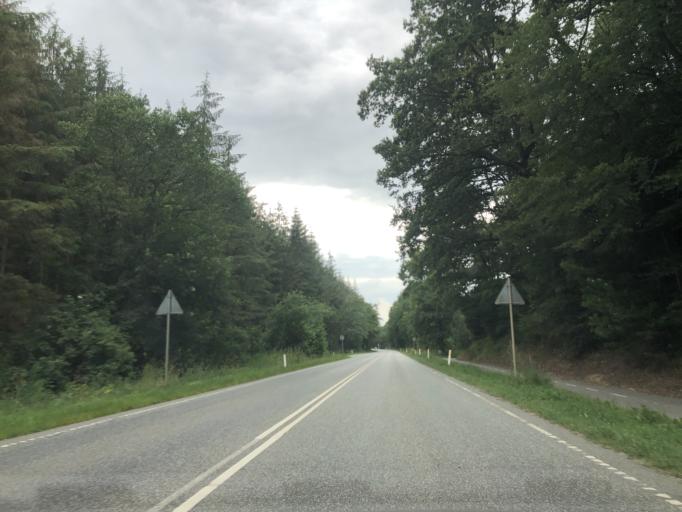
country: DK
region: Central Jutland
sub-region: Skanderborg Kommune
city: Ry
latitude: 56.1501
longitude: 9.7684
